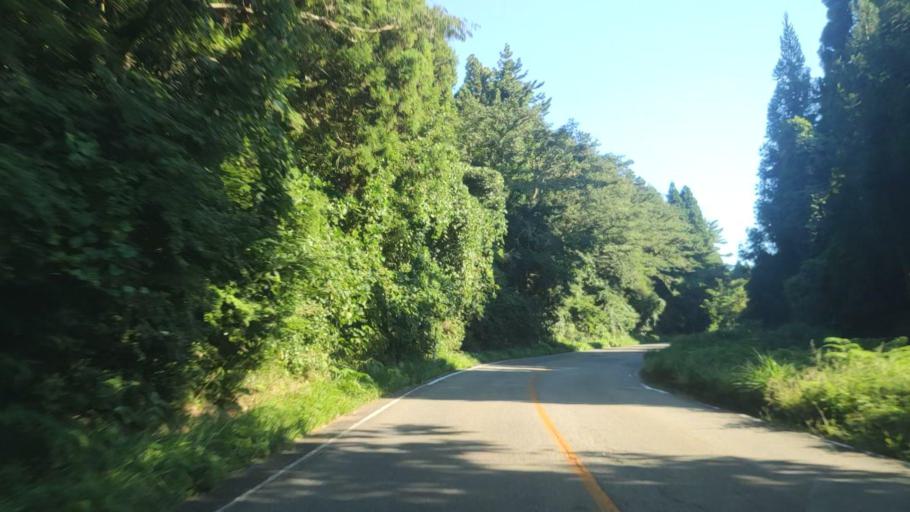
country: JP
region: Ishikawa
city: Nanao
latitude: 37.1061
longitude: 136.9470
